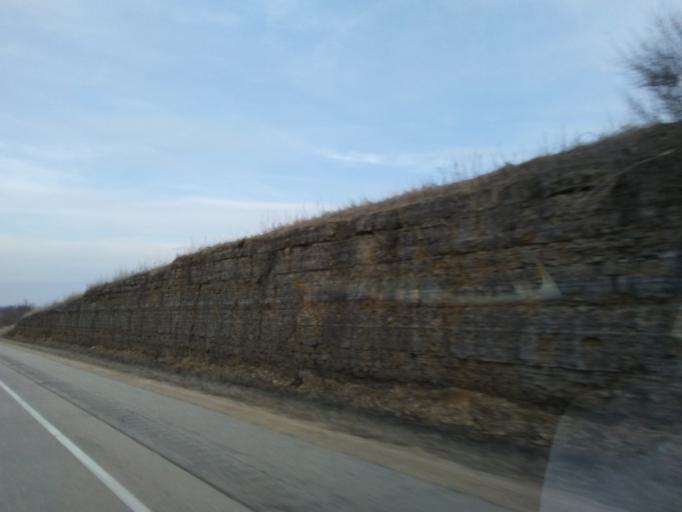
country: US
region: Wisconsin
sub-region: Dane County
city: Mount Horeb
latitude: 43.0102
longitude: -89.8065
